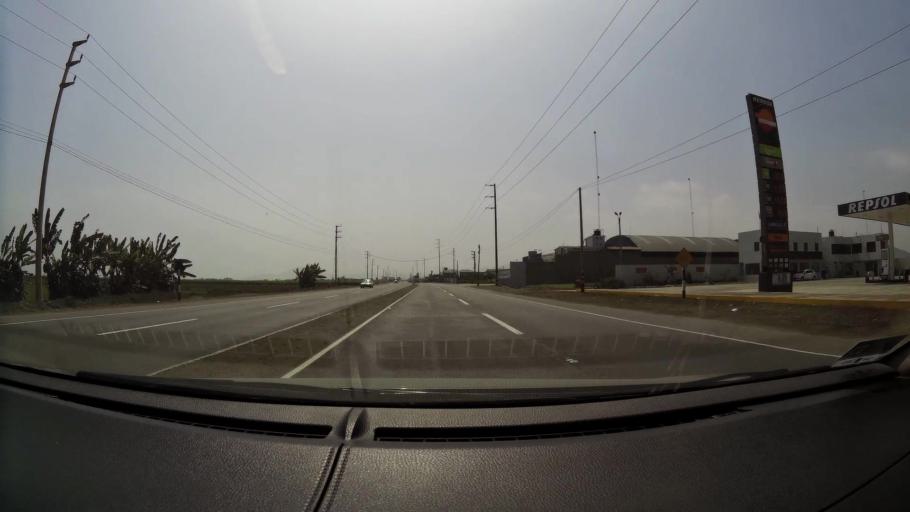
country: PE
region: Lima
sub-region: Provincia de Huaral
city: Chancay
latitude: -11.5418
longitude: -77.2809
